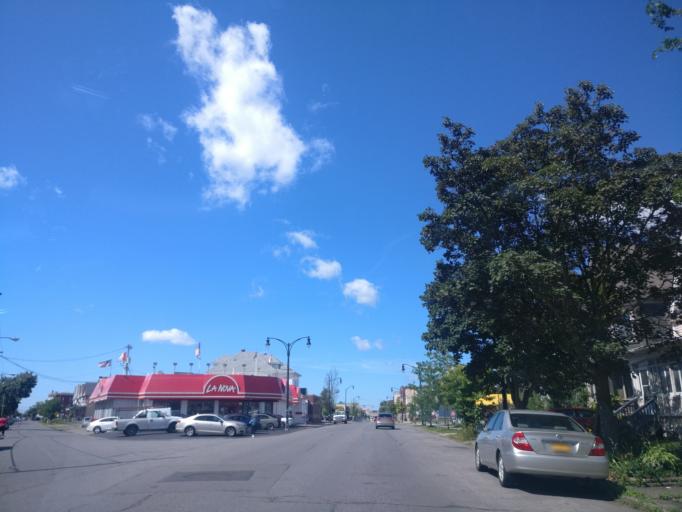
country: US
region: New York
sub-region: Erie County
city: Buffalo
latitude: 42.9154
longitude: -78.8873
